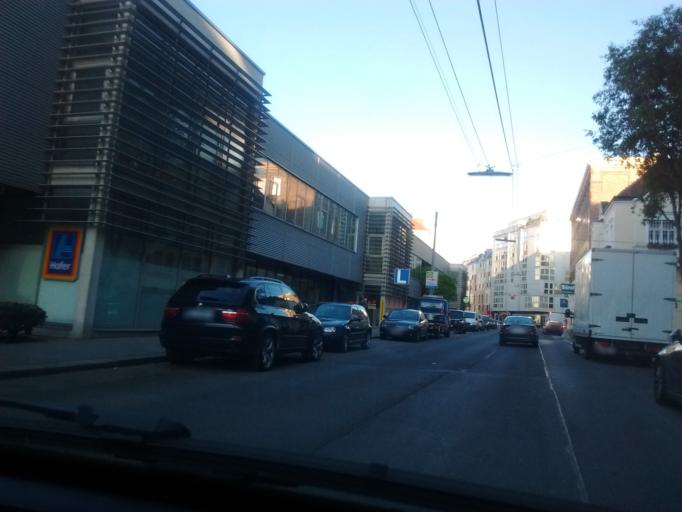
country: AT
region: Vienna
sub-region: Wien Stadt
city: Vienna
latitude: 48.1749
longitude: 16.3573
